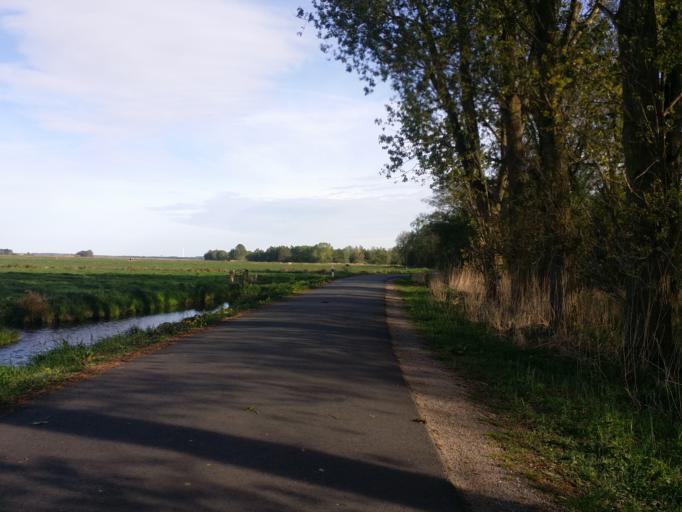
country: DE
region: Lower Saxony
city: Ritterhude
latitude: 53.1537
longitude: 8.7831
